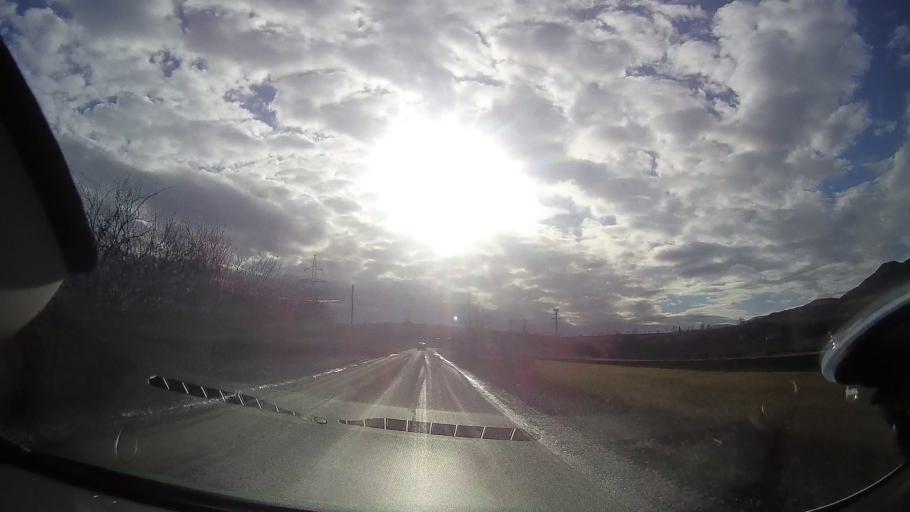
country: RO
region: Cluj
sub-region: Comuna Baisoara
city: Baisoara
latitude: 46.6243
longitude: 23.4531
